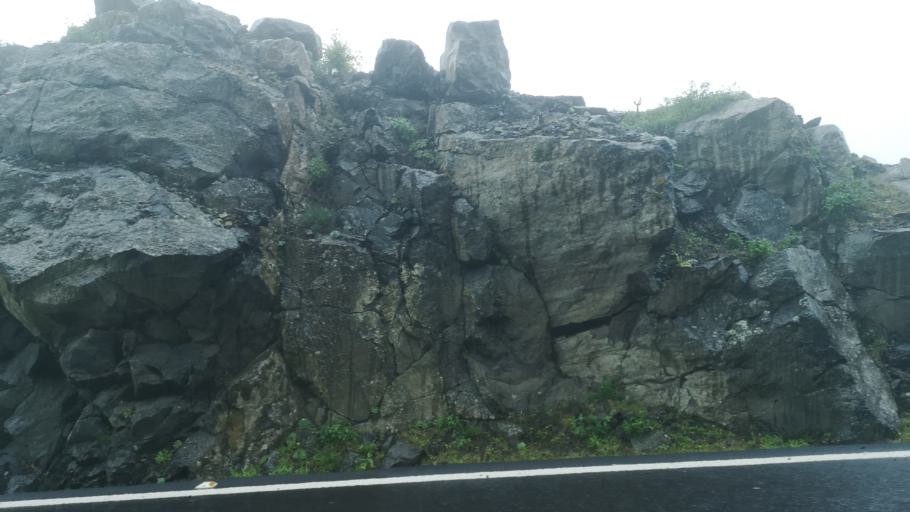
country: ES
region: Canary Islands
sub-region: Provincia de Santa Cruz de Tenerife
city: Alajero
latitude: 28.1000
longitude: -17.2023
